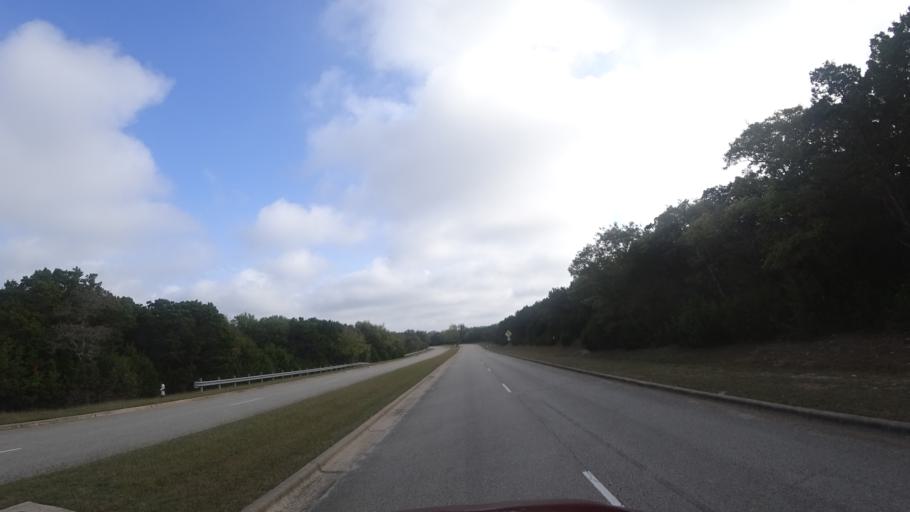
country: US
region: Texas
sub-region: Williamson County
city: Anderson Mill
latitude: 30.4024
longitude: -97.8404
